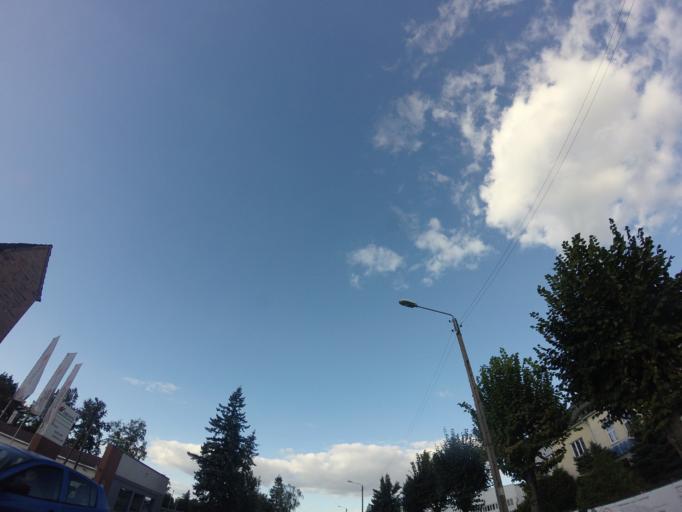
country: PL
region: Greater Poland Voivodeship
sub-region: Powiat nowotomyski
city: Nowy Tomysl
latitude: 52.3049
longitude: 16.1284
